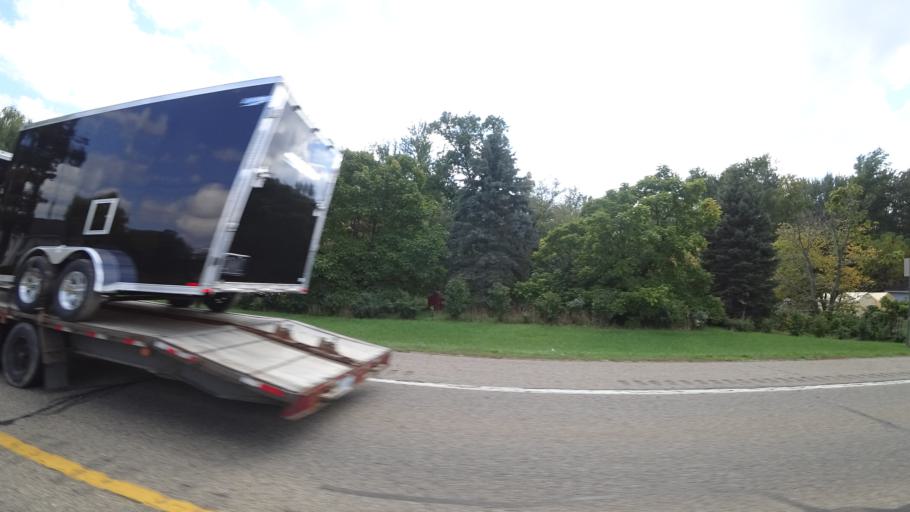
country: US
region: Michigan
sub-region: Branch County
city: Union City
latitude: 42.1057
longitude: -85.0614
